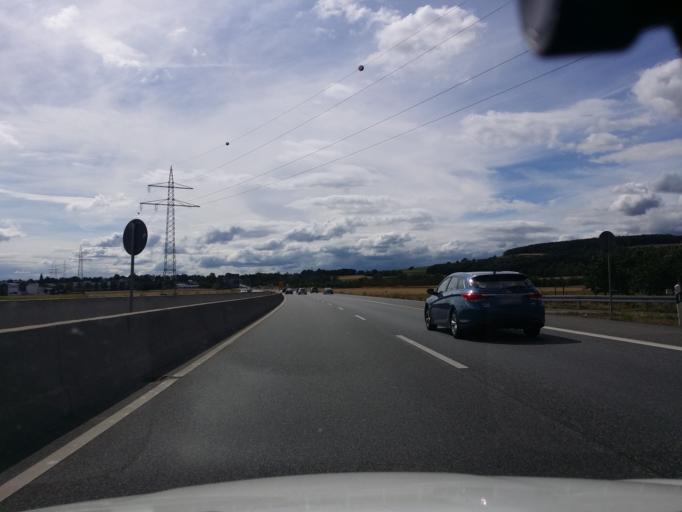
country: DE
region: Hesse
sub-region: Regierungsbezirk Darmstadt
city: Walluf
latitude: 50.0498
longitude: 8.1709
